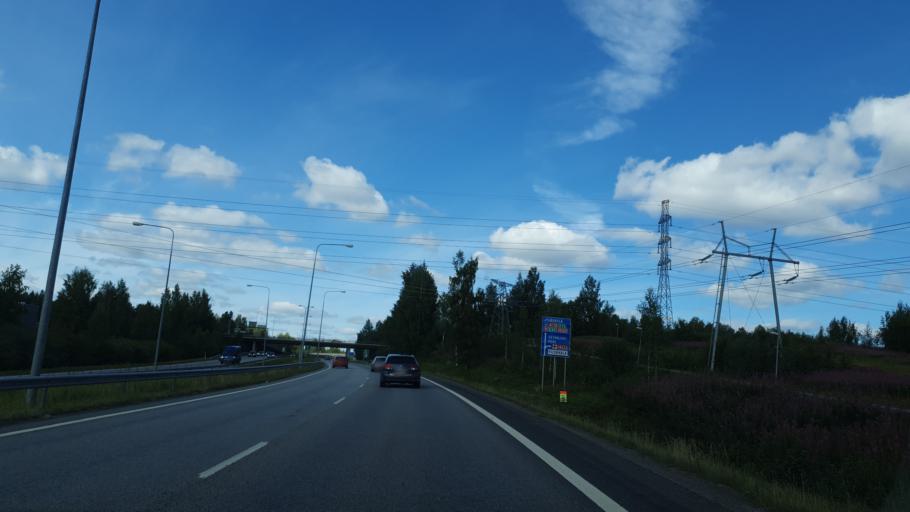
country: FI
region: Central Finland
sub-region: Jyvaeskylae
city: Jyvaeskylae
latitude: 62.2155
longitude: 25.7252
